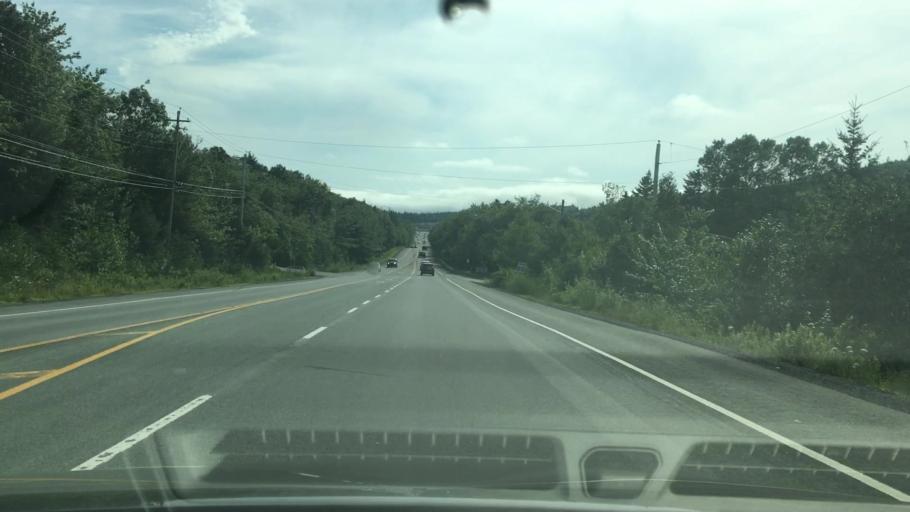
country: CA
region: Nova Scotia
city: Dartmouth
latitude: 44.7102
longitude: -63.8426
